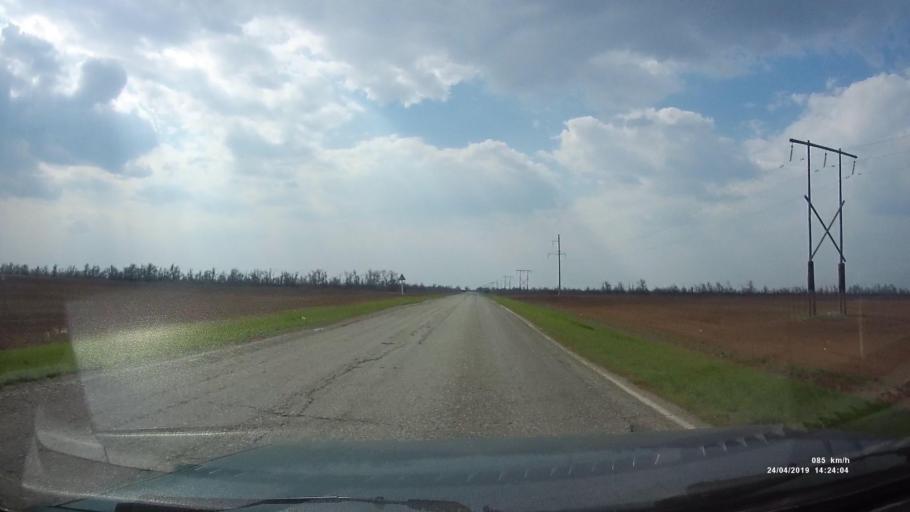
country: RU
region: Kalmykiya
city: Arshan'
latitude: 46.3264
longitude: 44.1050
